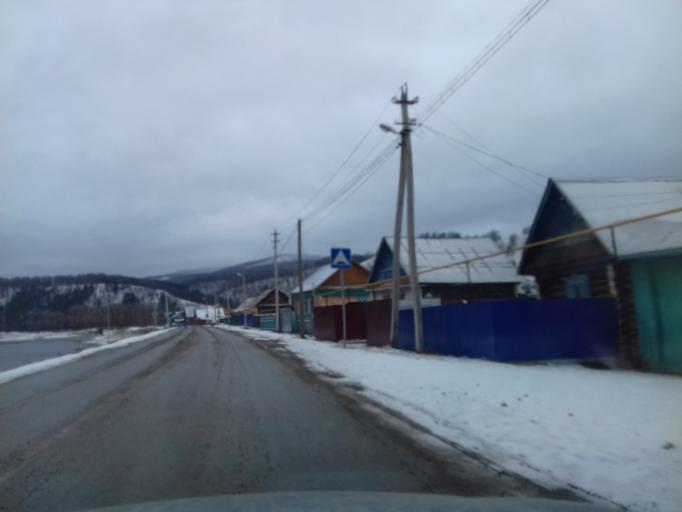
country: RU
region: Bashkortostan
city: Starosubkhangulovo
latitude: 53.0964
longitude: 57.4379
